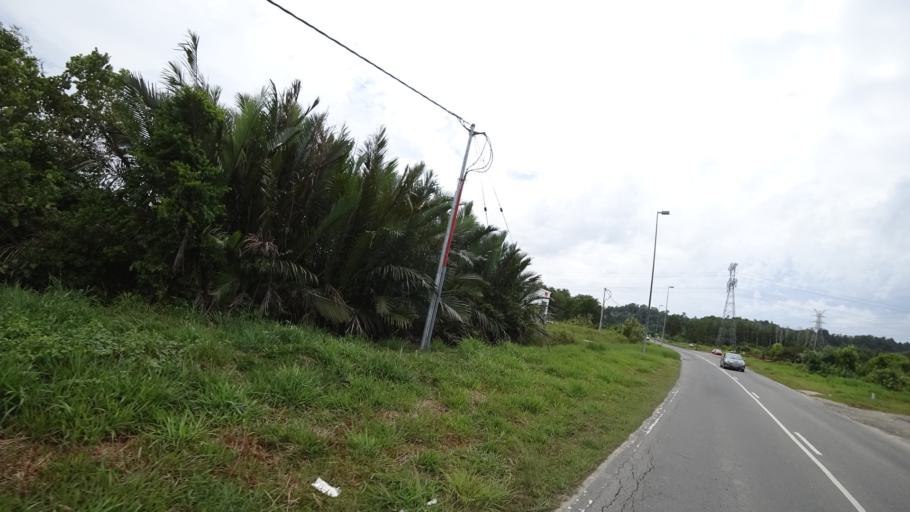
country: BN
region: Tutong
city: Tutong
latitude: 4.8215
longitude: 114.6828
